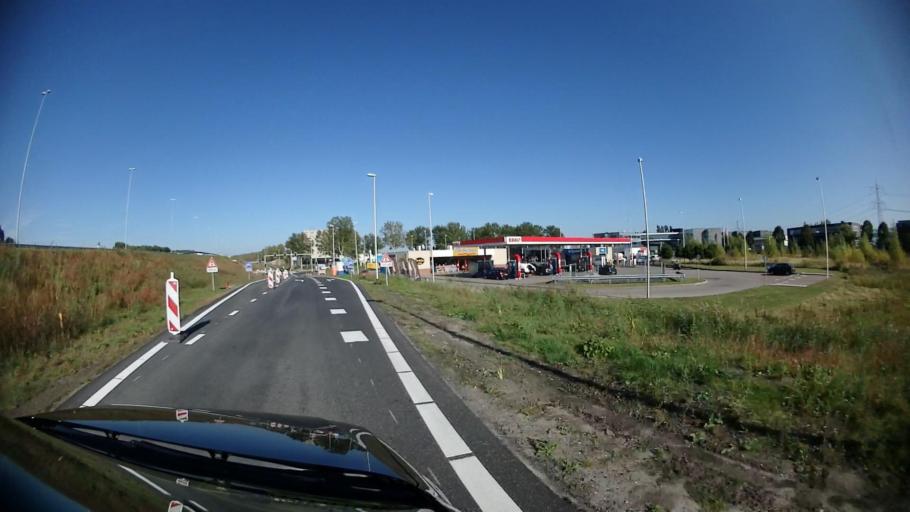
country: NL
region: Flevoland
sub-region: Gemeente Almere
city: Almere Stad
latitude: 52.3487
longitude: 5.1737
